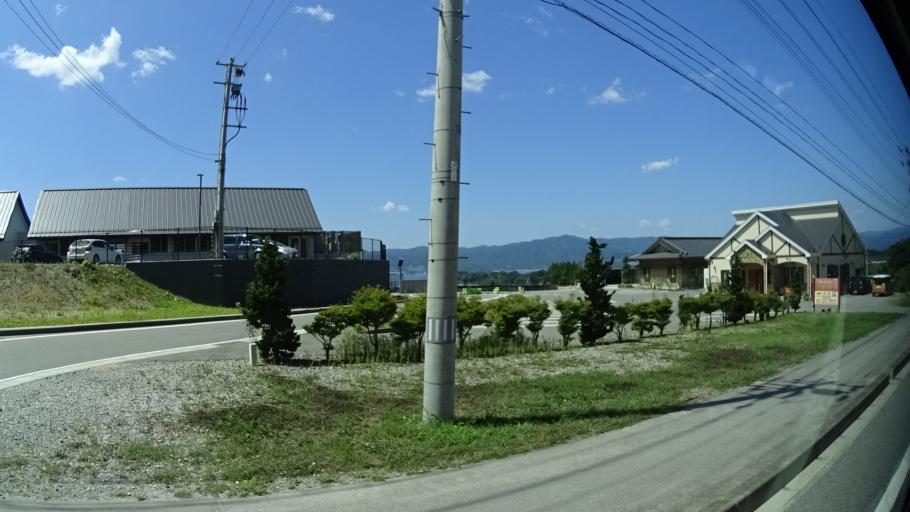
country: JP
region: Iwate
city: Ofunato
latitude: 39.0085
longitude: 141.6789
